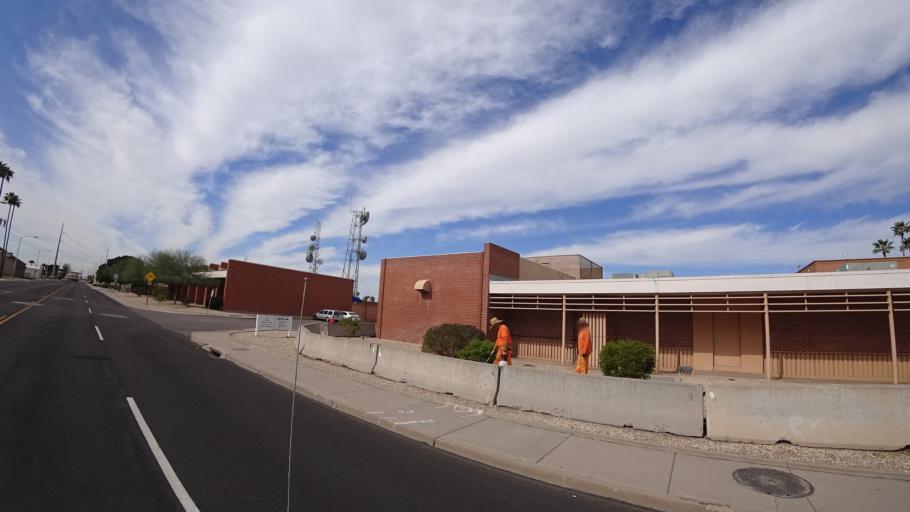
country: US
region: Arizona
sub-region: Maricopa County
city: Phoenix
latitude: 33.4732
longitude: -112.1029
